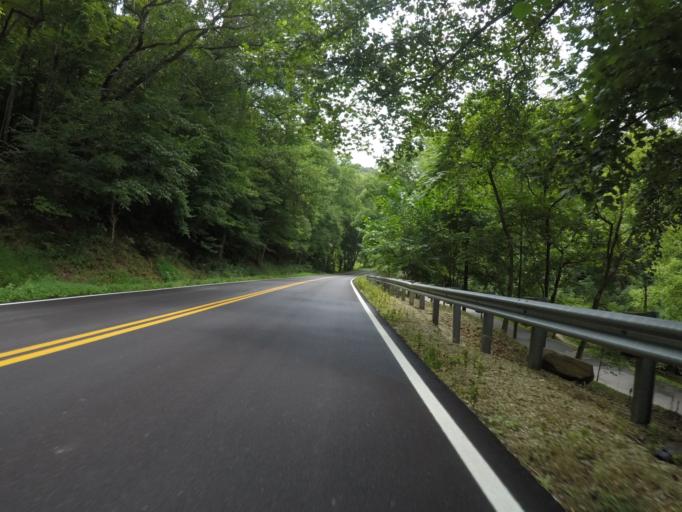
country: US
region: Kentucky
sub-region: Boyd County
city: Catlettsburg
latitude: 38.4278
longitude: -82.6285
